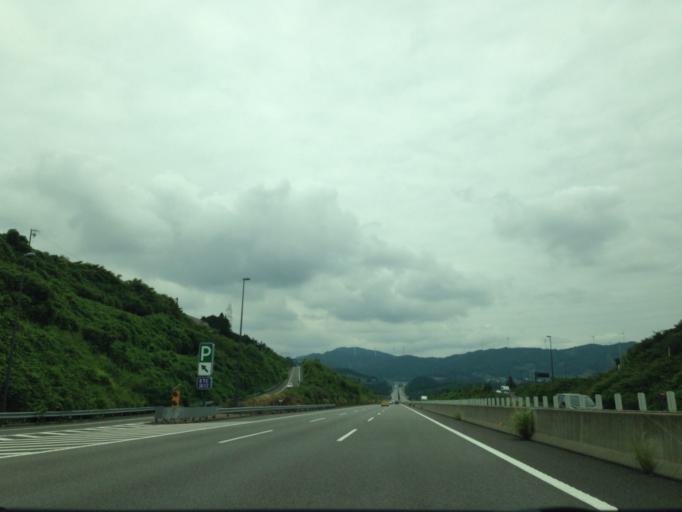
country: JP
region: Shizuoka
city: Hamakita
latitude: 34.8403
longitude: 137.7564
